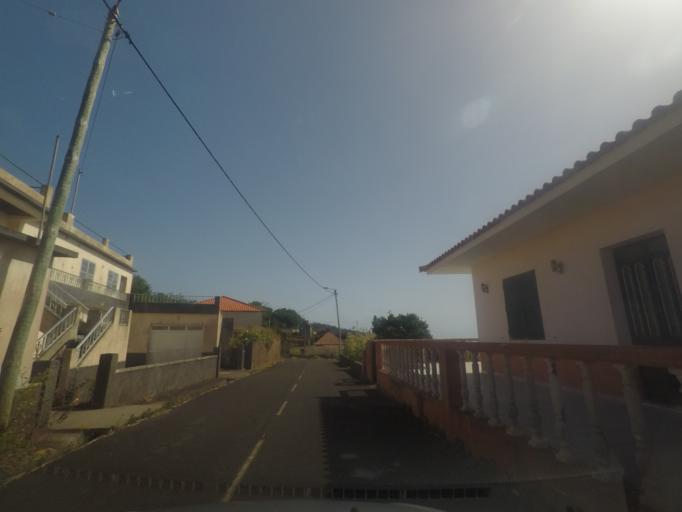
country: PT
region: Madeira
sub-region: Calheta
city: Faja da Ovelha
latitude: 32.8275
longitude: -17.2336
